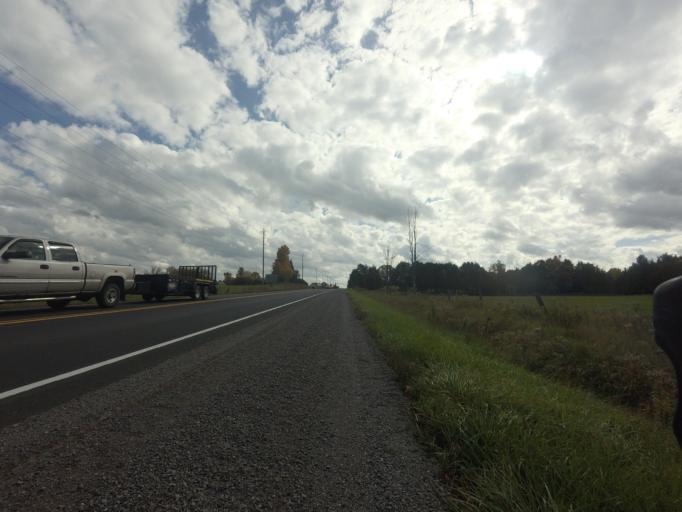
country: CA
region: Ontario
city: Pembroke
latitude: 45.5631
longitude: -77.1174
